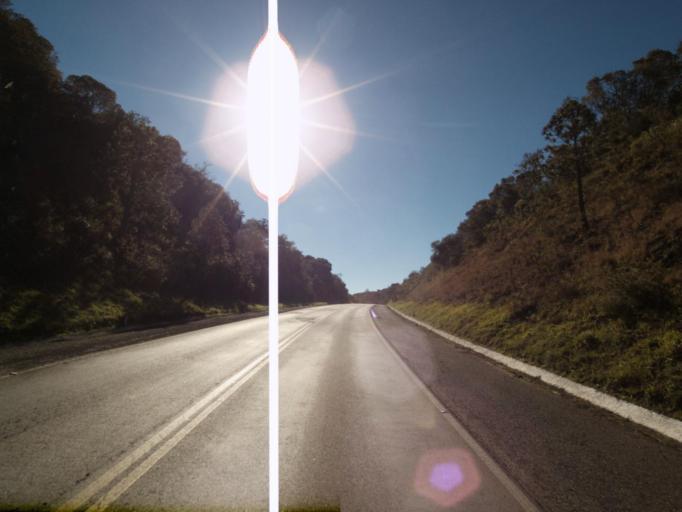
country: BR
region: Santa Catarina
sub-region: Concordia
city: Concordia
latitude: -26.9555
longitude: -51.8351
